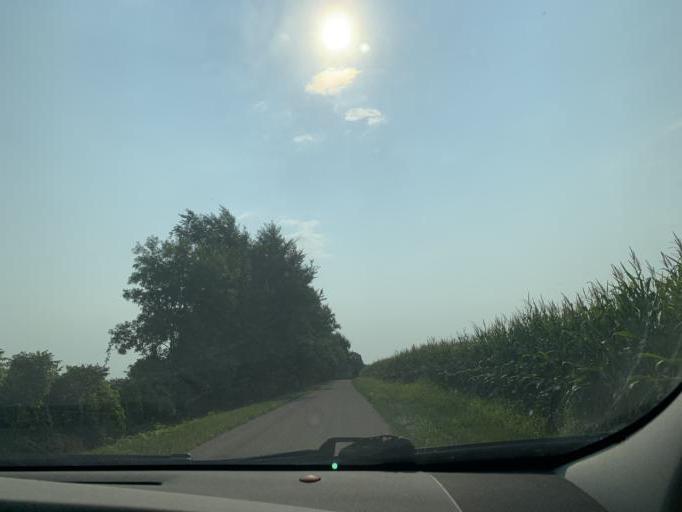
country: US
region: Illinois
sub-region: Whiteside County
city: Morrison
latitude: 41.8607
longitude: -89.8756
